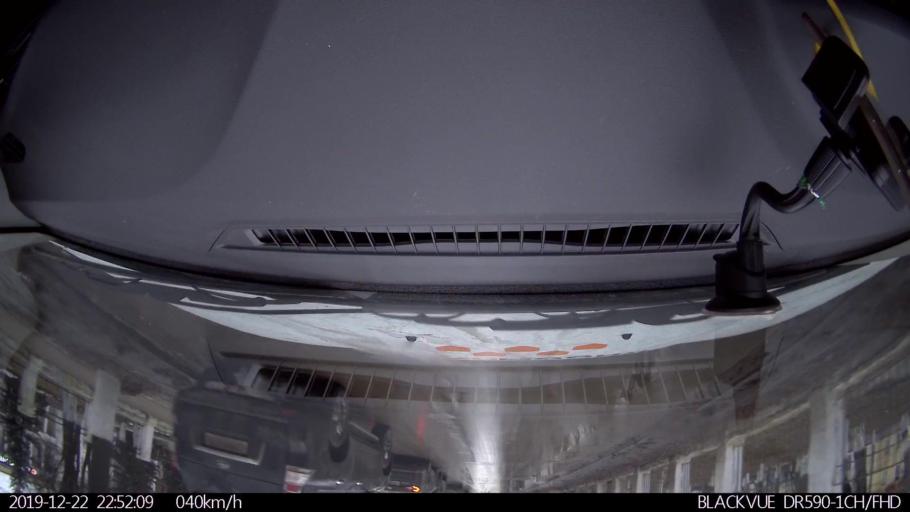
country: RU
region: Nizjnij Novgorod
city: Gorbatovka
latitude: 56.2441
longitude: 43.8602
